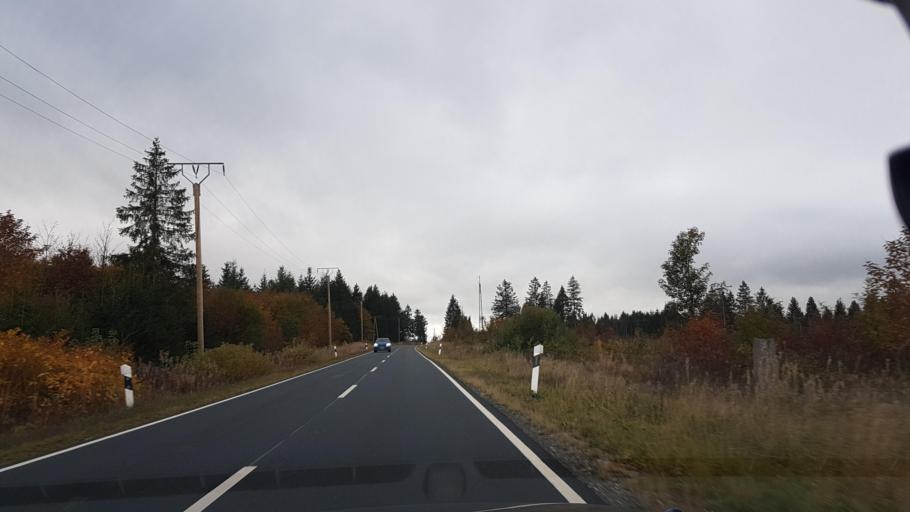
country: DE
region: Lower Saxony
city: Clausthal-Zellerfeld
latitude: 51.8252
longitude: 10.3658
